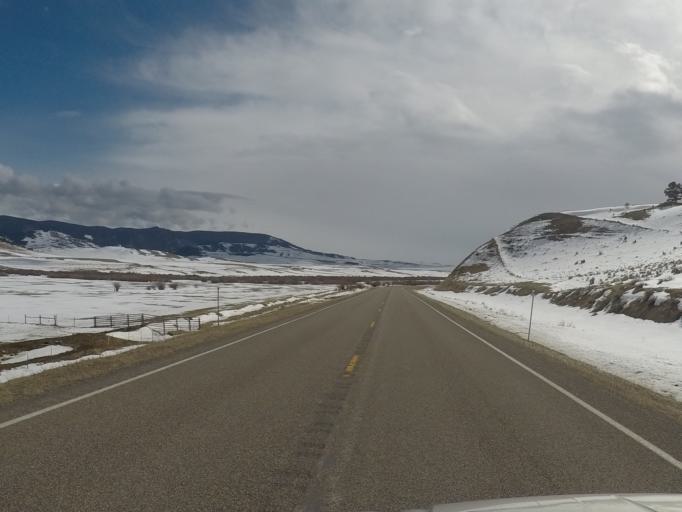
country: US
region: Montana
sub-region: Meagher County
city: White Sulphur Springs
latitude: 46.5872
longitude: -110.8428
